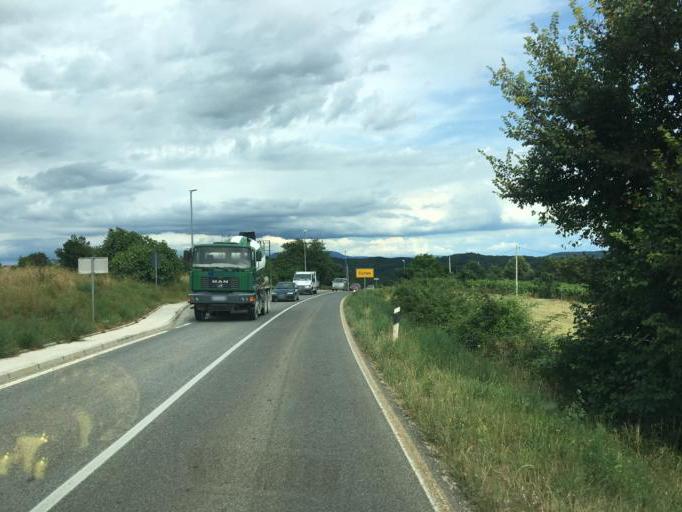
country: HR
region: Istarska
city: Pazin
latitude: 45.2542
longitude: 13.8768
